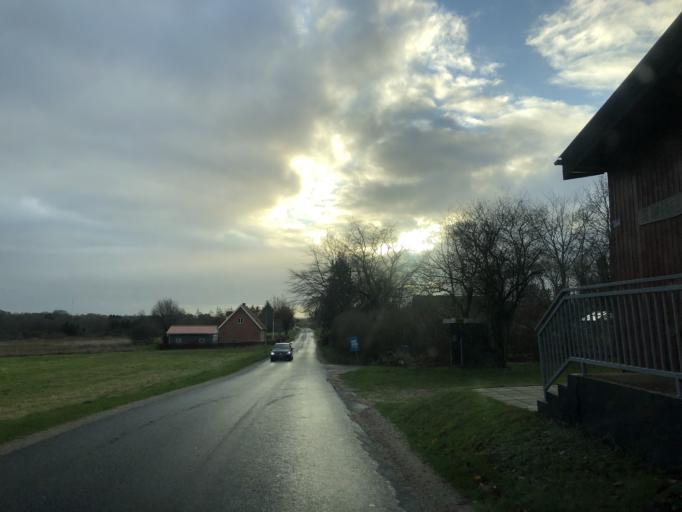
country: DK
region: Central Jutland
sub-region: Viborg Kommune
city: Viborg
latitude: 56.4814
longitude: 9.3441
